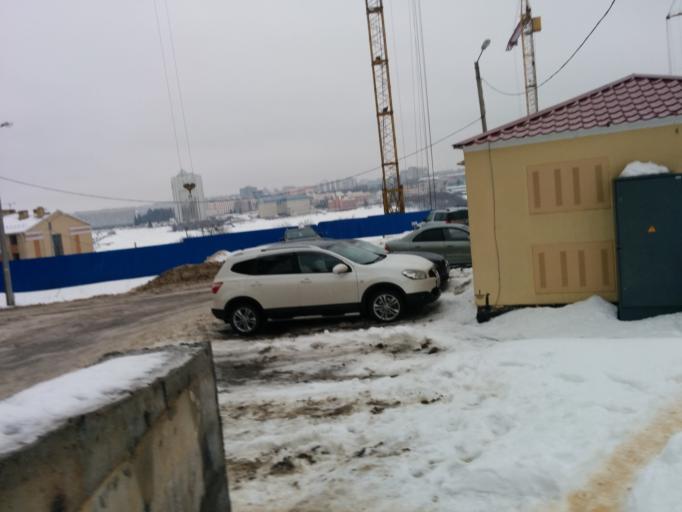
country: RU
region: Chuvashia
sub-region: Cheboksarskiy Rayon
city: Cheboksary
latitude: 56.1425
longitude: 47.2308
